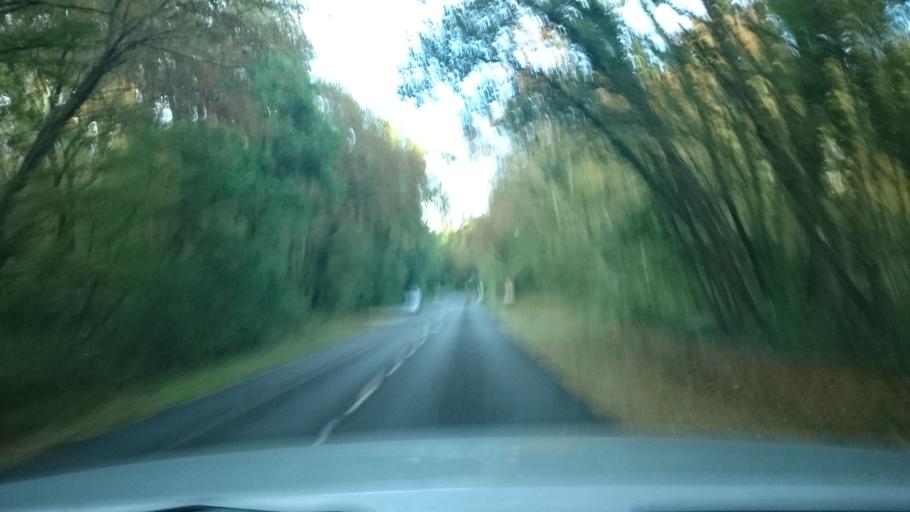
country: FR
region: Ile-de-France
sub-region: Departement de Seine-et-Marne
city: Samois-sur-Seine
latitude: 48.4829
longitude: 2.7495
